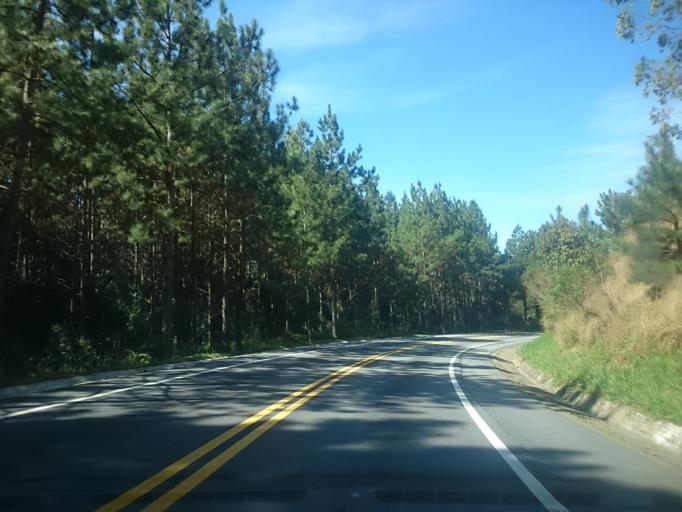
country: BR
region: Santa Catarina
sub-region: Santo Amaro Da Imperatriz
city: Santo Amaro da Imperatriz
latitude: -27.7092
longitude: -48.9503
